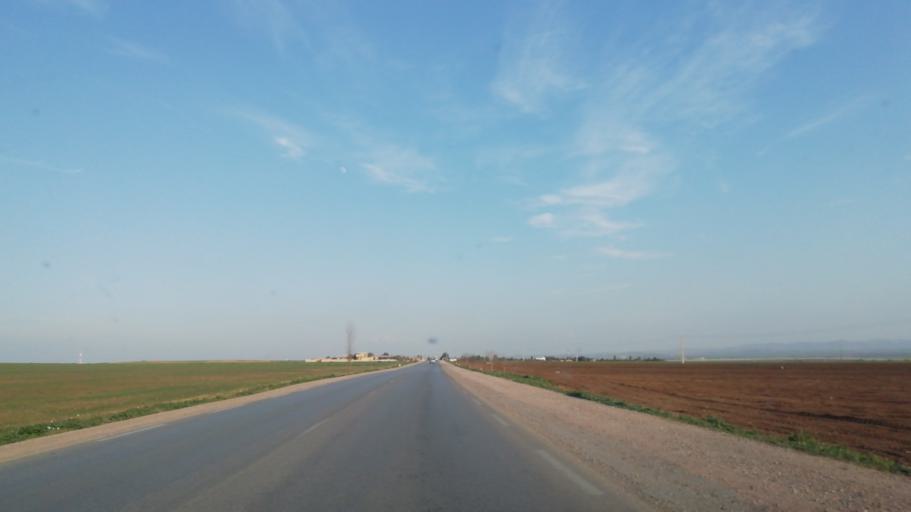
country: DZ
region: Relizane
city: Djidiouia
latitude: 35.8944
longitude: 0.6526
